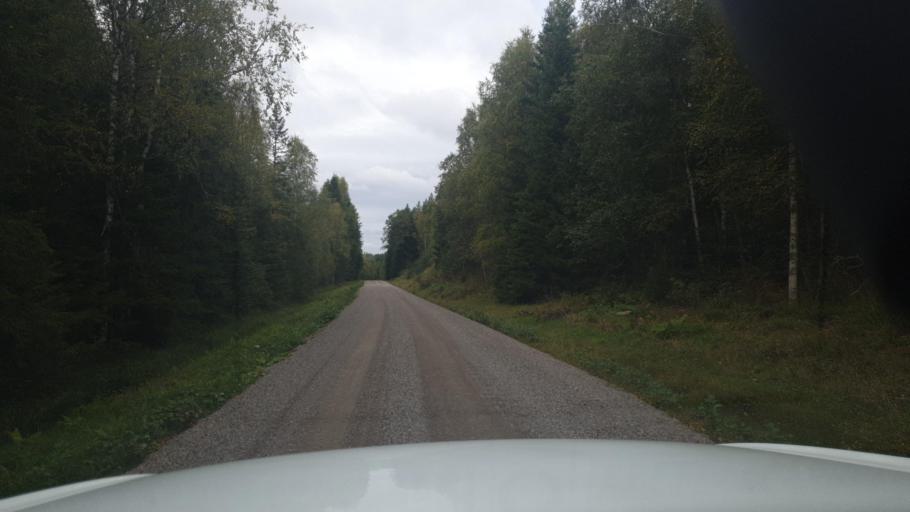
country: SE
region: Vaermland
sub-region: Eda Kommun
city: Charlottenberg
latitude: 60.0519
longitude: 12.6299
